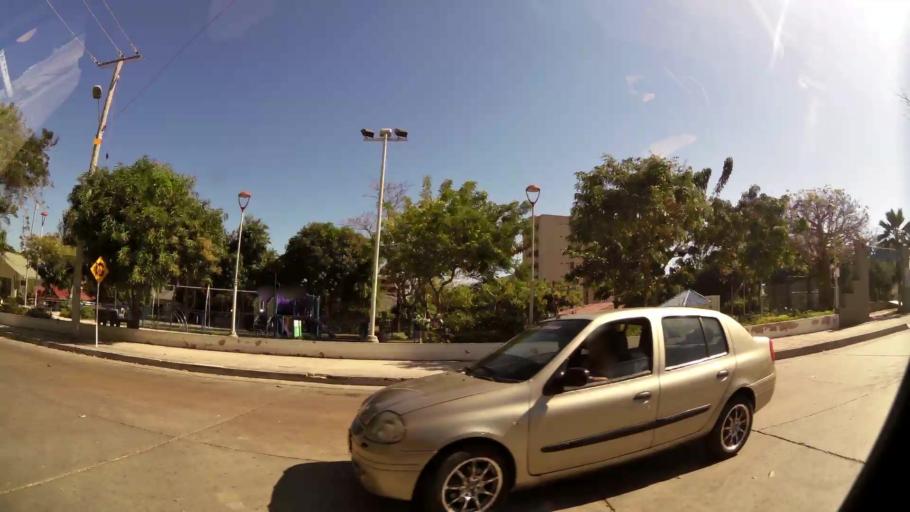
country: CO
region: Atlantico
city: Barranquilla
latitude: 11.0015
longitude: -74.7913
